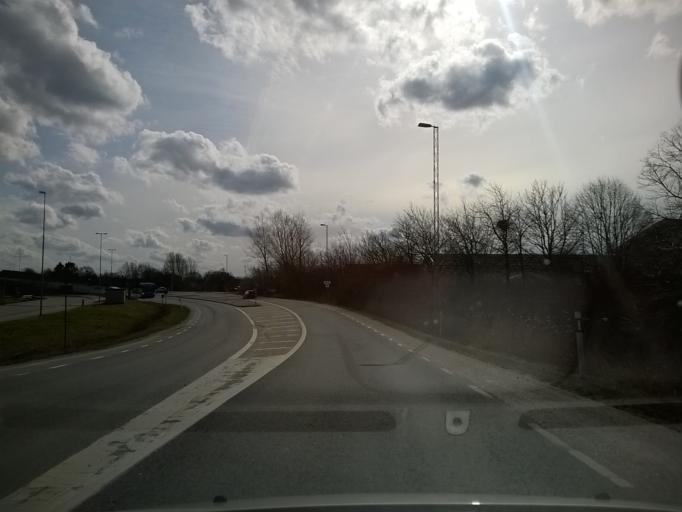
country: SE
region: Vaestra Goetaland
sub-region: Stenungsunds Kommun
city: Stora Hoga
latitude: 57.9887
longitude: 11.8300
